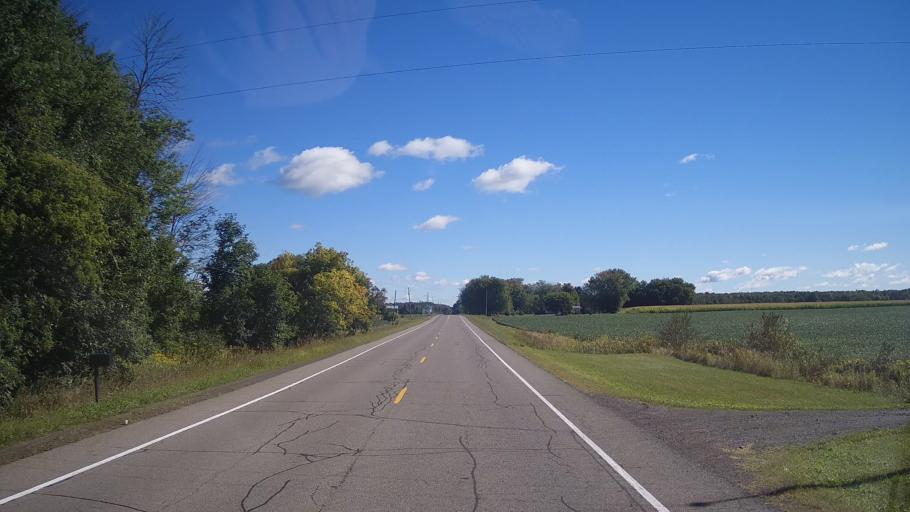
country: US
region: New York
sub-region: St. Lawrence County
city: Ogdensburg
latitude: 44.9459
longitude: -75.2937
